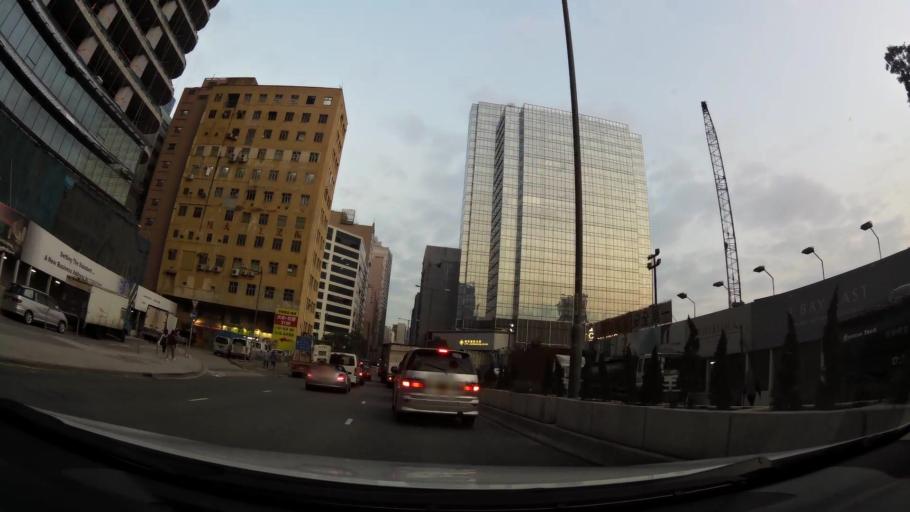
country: HK
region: Kowloon City
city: Kowloon
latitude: 22.3147
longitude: 114.2165
